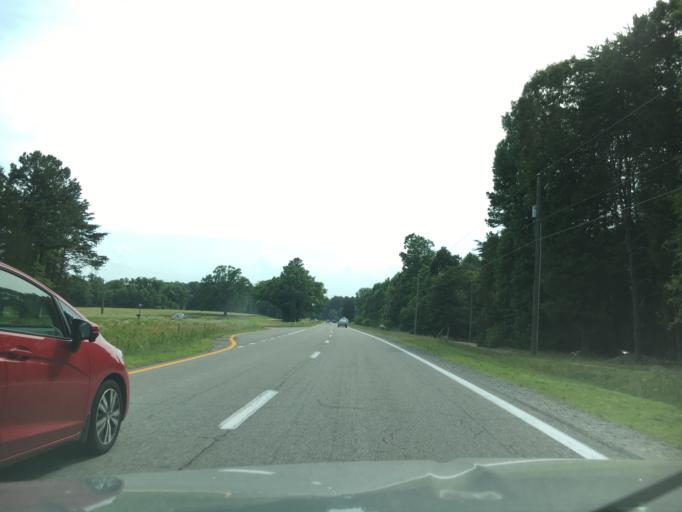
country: US
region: Virginia
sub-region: Halifax County
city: South Boston
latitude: 36.7614
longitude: -78.8341
